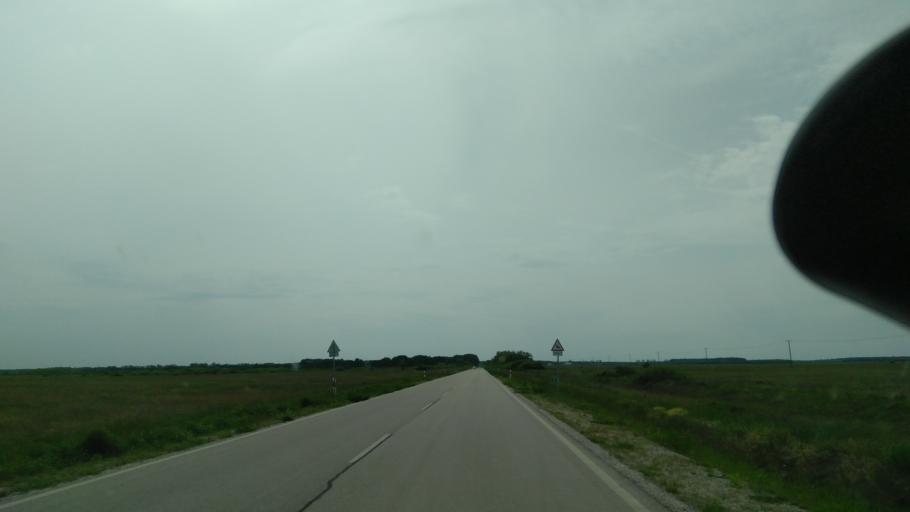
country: HU
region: Bekes
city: Mehkerek
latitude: 46.8666
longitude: 21.4866
